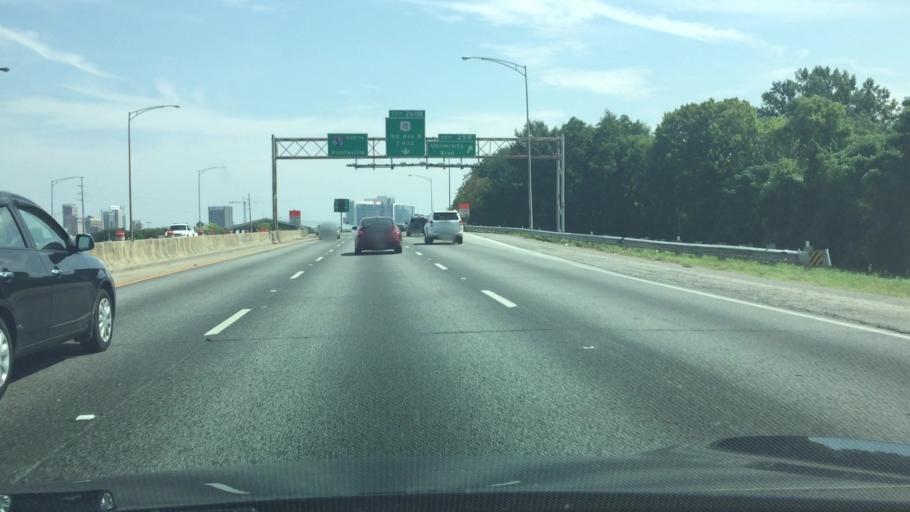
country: US
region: Alabama
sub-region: Jefferson County
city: Birmingham
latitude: 33.4959
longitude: -86.8164
